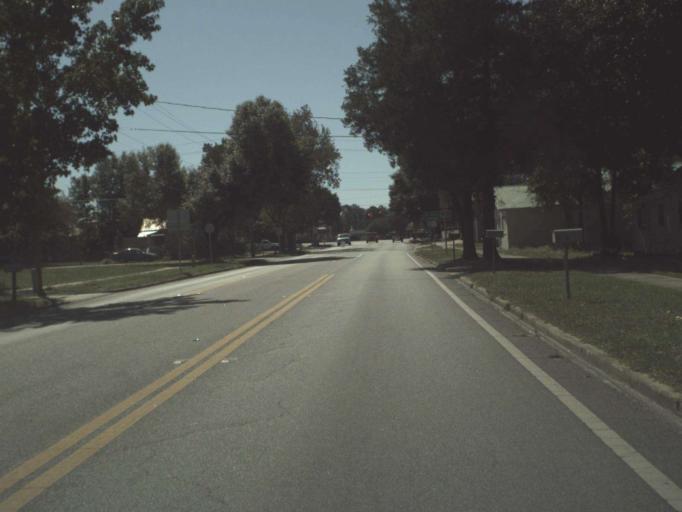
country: US
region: Florida
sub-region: Walton County
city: DeFuniak Springs
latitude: 30.7232
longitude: -86.1153
